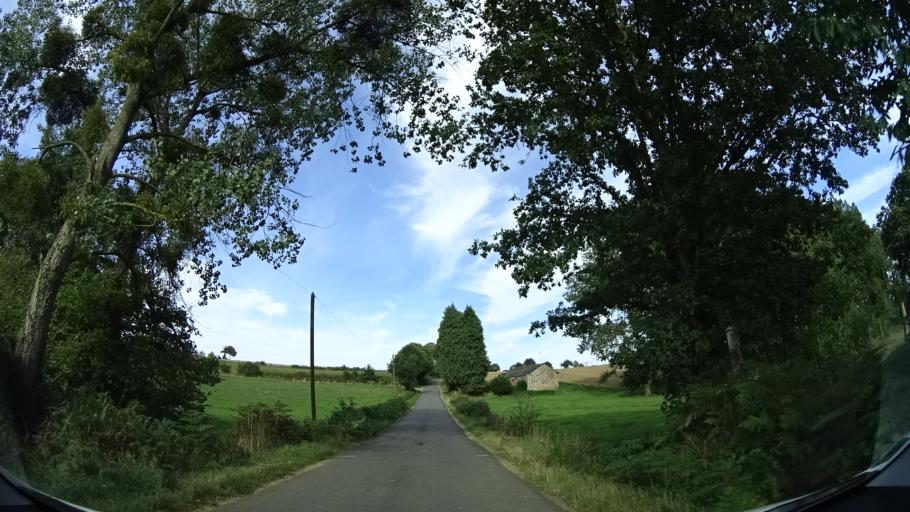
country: FR
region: Brittany
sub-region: Departement d'Ille-et-Vilaine
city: Romagne
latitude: 48.3136
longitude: -1.2861
